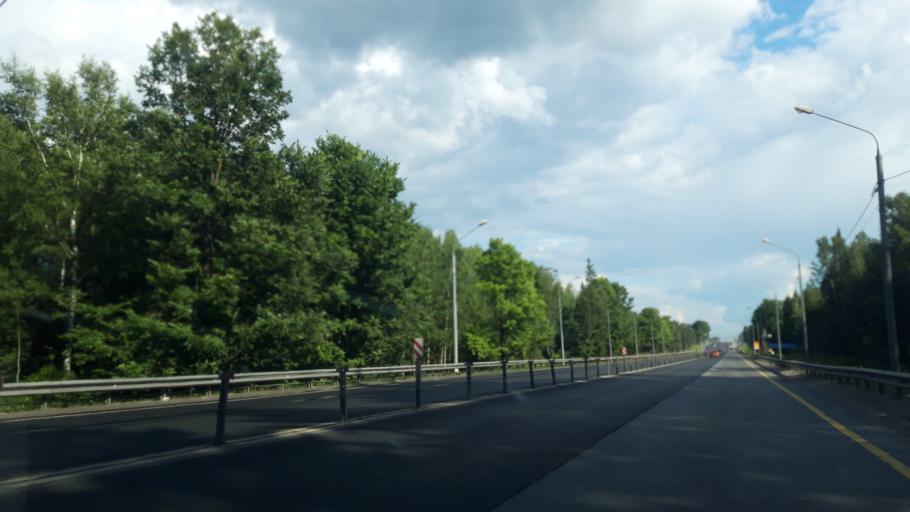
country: RU
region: Moskovskaya
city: Solnechnogorsk
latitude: 56.2572
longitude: 36.8650
